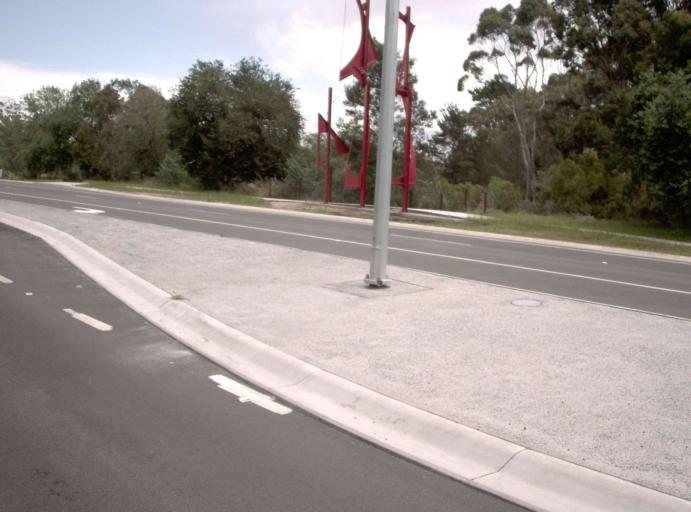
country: AU
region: Victoria
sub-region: Wellington
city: Sale
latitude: -38.1123
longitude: 147.0568
